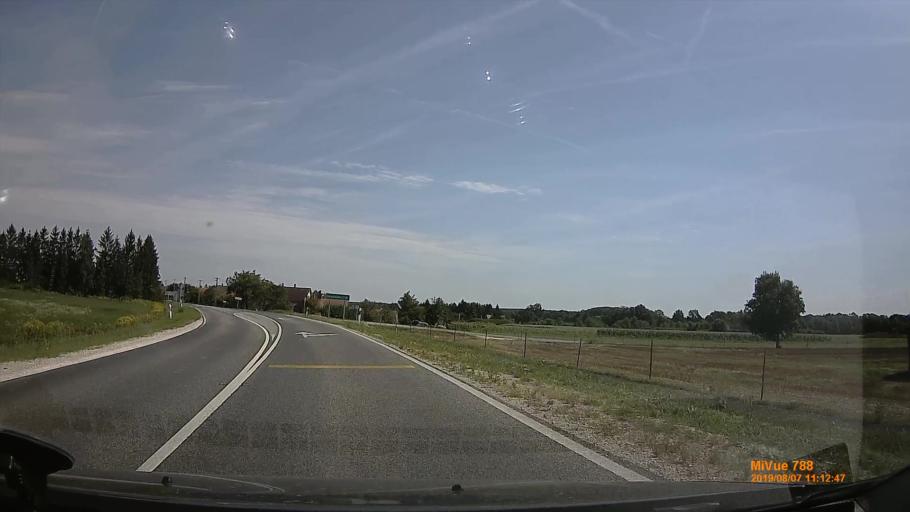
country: HU
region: Zala
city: Lenti
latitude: 46.6944
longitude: 16.5447
